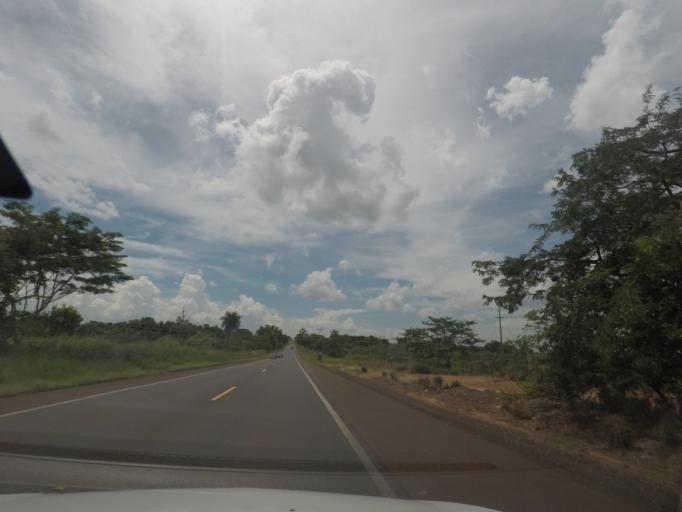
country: BR
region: Sao Paulo
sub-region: Barretos
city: Barretos
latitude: -20.3709
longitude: -48.6455
